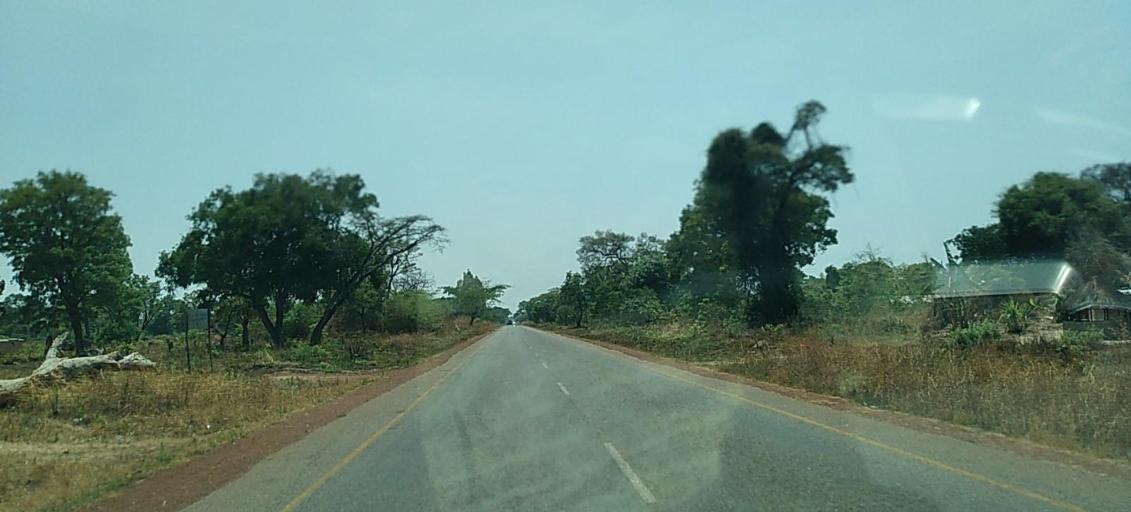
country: ZM
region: North-Western
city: Solwezi
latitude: -12.3954
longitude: 26.1592
